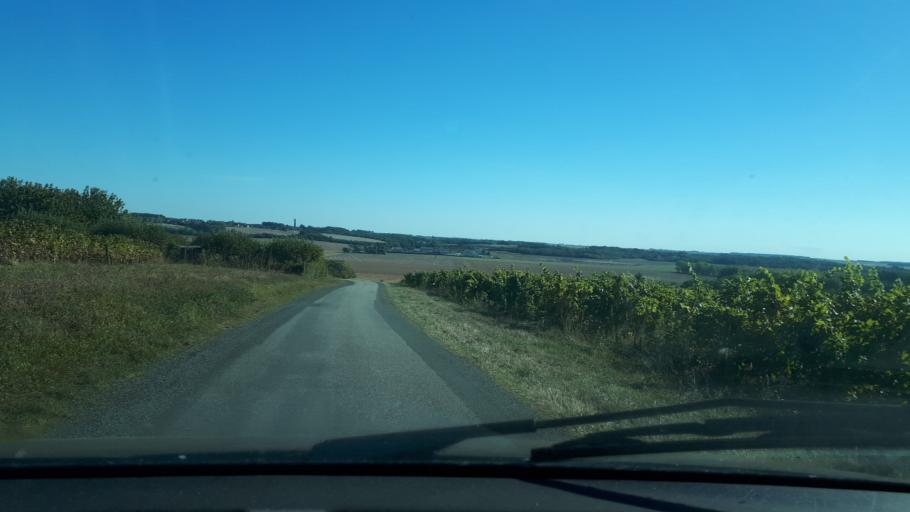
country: FR
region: Centre
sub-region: Departement du Loir-et-Cher
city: Naveil
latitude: 47.7992
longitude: 1.0191
